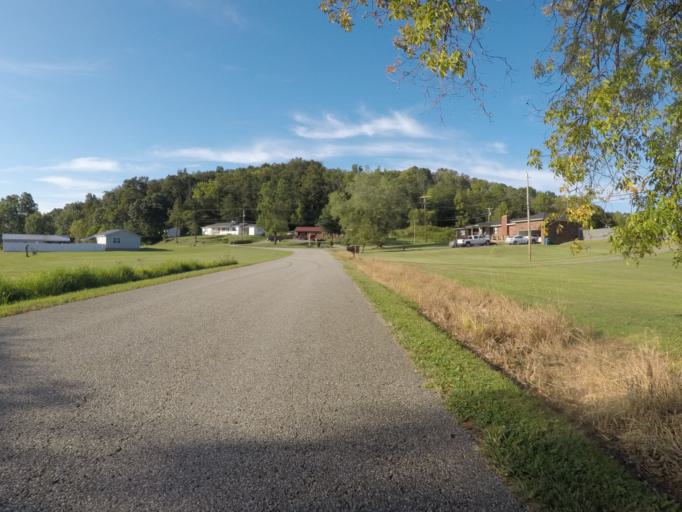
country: US
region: West Virginia
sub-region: Cabell County
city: Huntington
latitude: 38.5023
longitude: -82.4879
